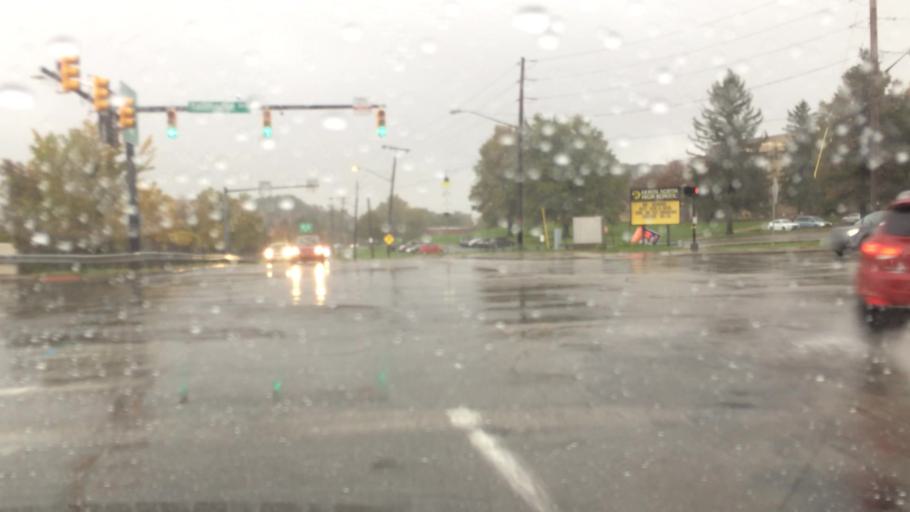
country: US
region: Ohio
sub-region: Summit County
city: Akron
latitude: 41.1021
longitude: -81.4995
